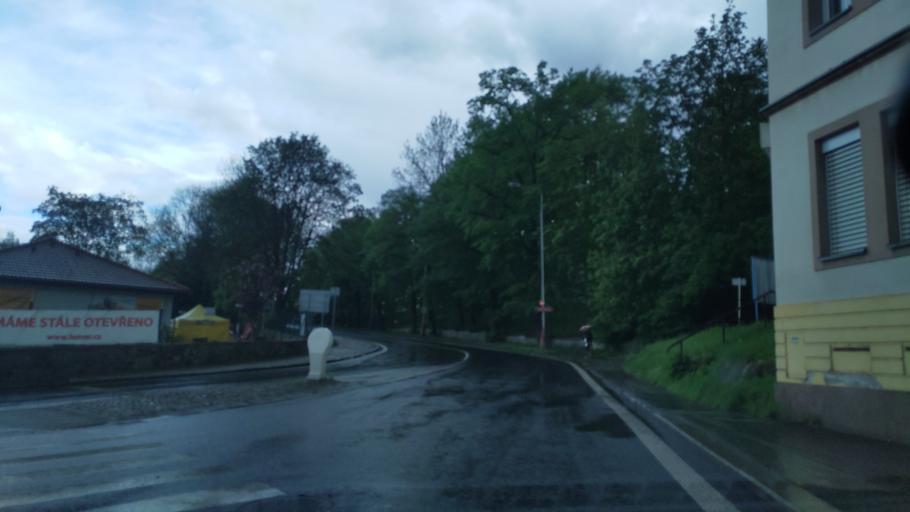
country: CZ
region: Ustecky
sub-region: Okres Usti nad Labem
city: Usti nad Labem
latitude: 50.6754
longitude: 14.0152
